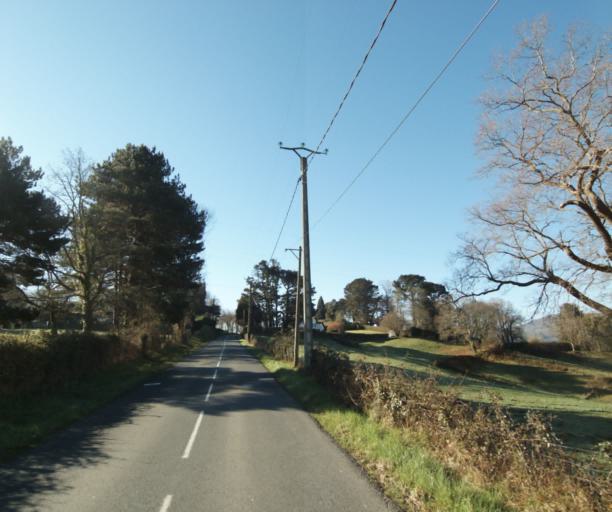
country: FR
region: Aquitaine
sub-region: Departement des Pyrenees-Atlantiques
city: Ciboure
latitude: 43.3561
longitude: -1.6659
